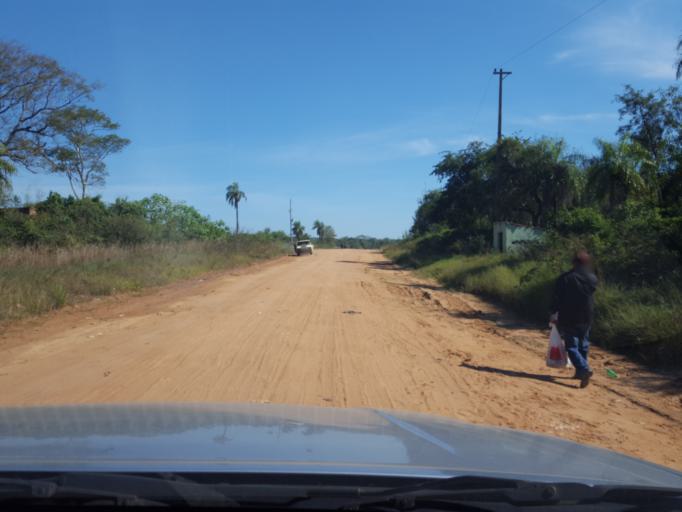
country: PY
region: Cordillera
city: Tobati
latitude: -25.2572
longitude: -57.0950
